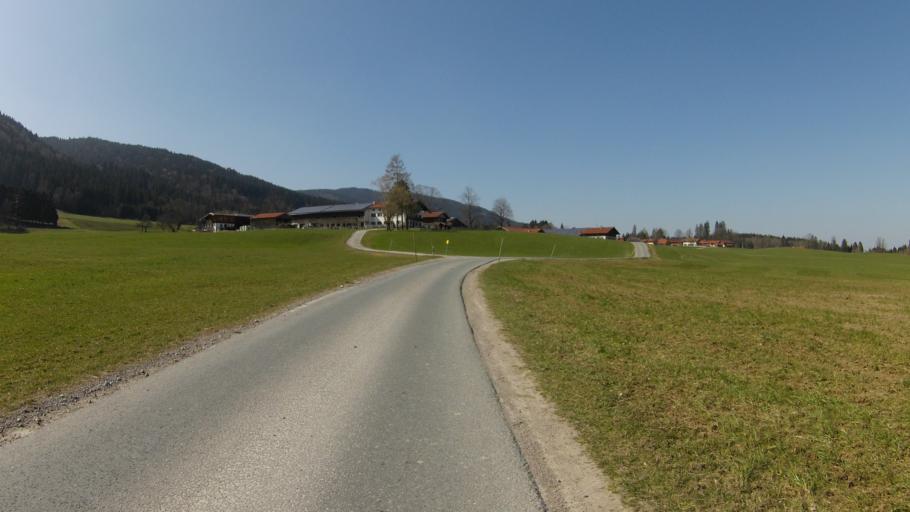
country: DE
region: Bavaria
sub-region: Upper Bavaria
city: Fischbachau
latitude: 47.7205
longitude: 11.9309
